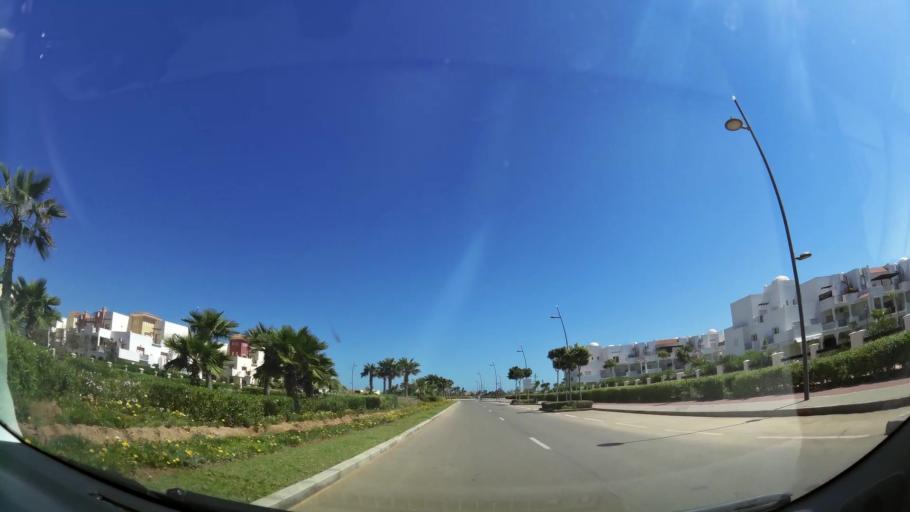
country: MA
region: Oriental
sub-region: Berkane-Taourirt
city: Madagh
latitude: 35.0982
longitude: -2.3004
